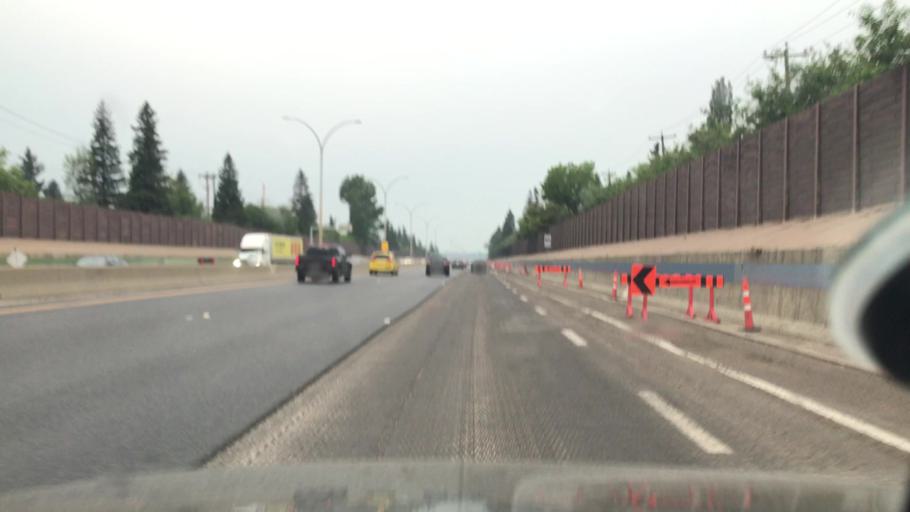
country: CA
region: Alberta
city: Edmonton
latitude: 53.4832
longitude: -113.5244
